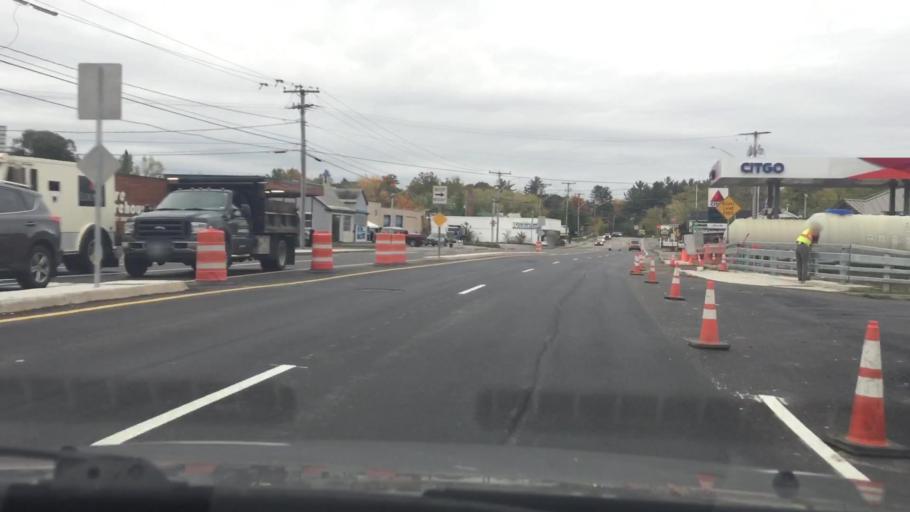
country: US
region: New Hampshire
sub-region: Cheshire County
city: Keene
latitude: 42.9212
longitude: -72.2758
